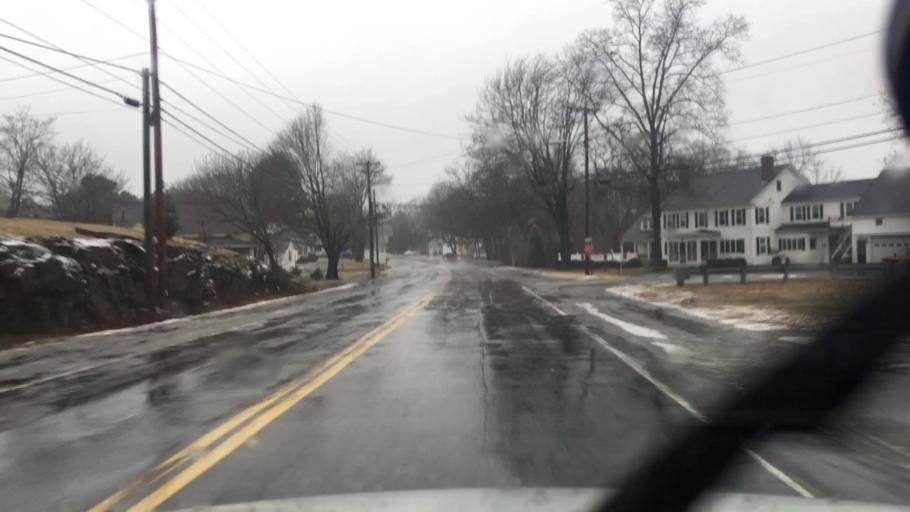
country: US
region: Maine
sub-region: York County
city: Saco
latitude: 43.4825
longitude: -70.4301
